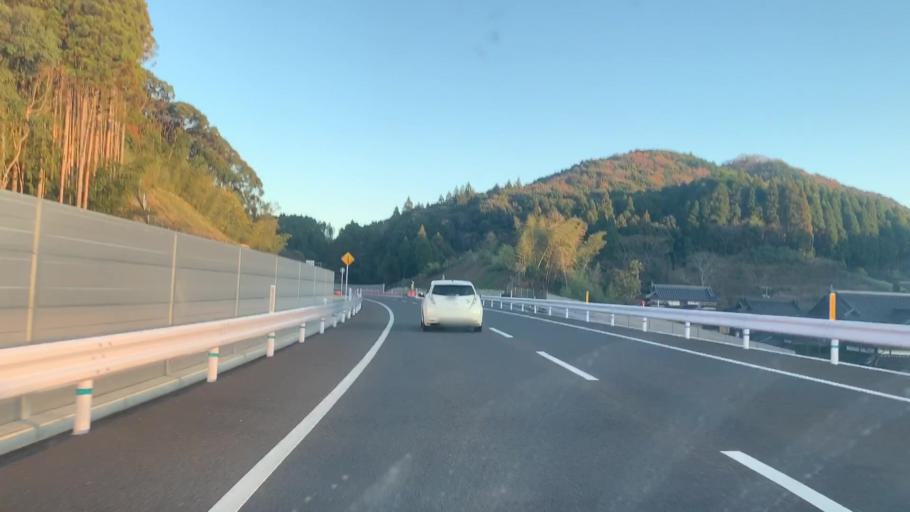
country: JP
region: Saga Prefecture
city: Takeocho-takeo
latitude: 33.2577
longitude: 129.9757
